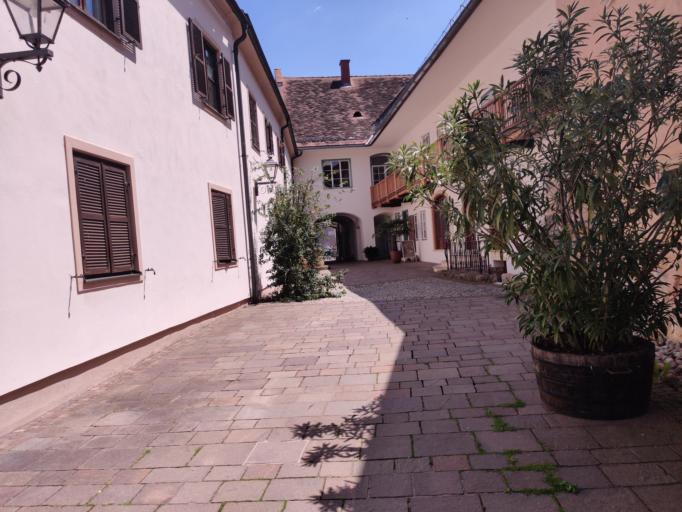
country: AT
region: Styria
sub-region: Politischer Bezirk Suedoststeiermark
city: Bad Radkersburg
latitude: 46.6864
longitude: 15.9852
